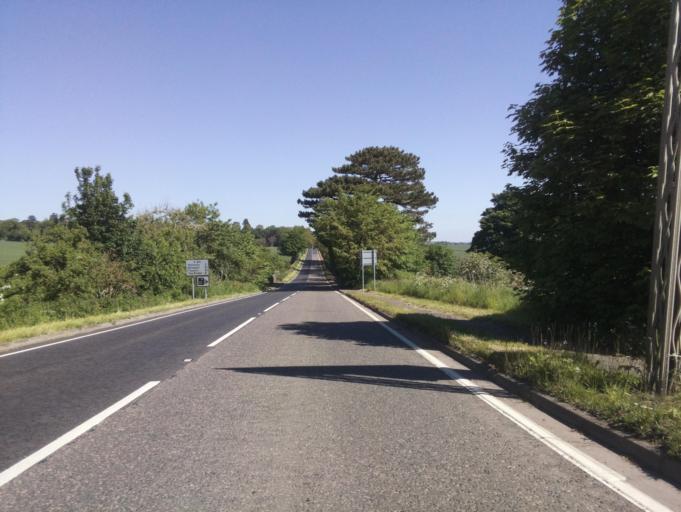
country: GB
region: Scotland
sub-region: Fife
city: Balmullo
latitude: 56.3491
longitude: -2.9416
